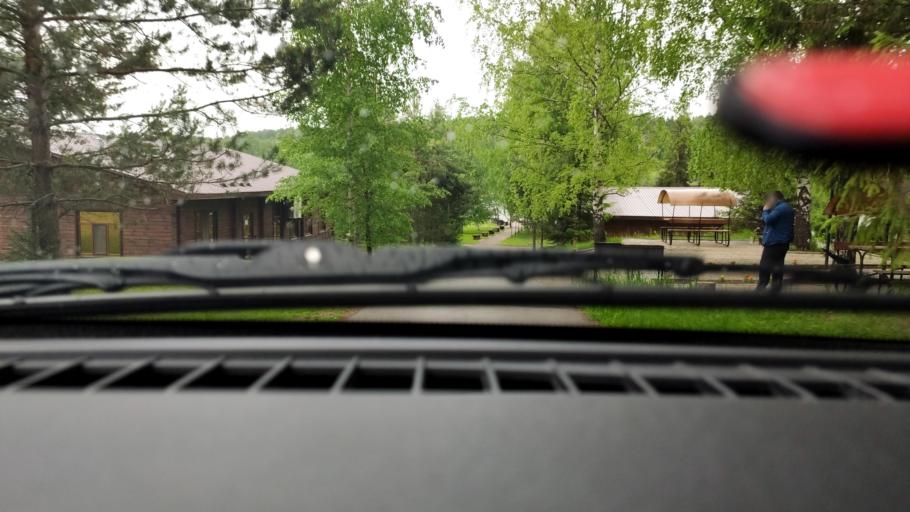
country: RU
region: Perm
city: Karagay
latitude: 58.2371
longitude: 54.8747
